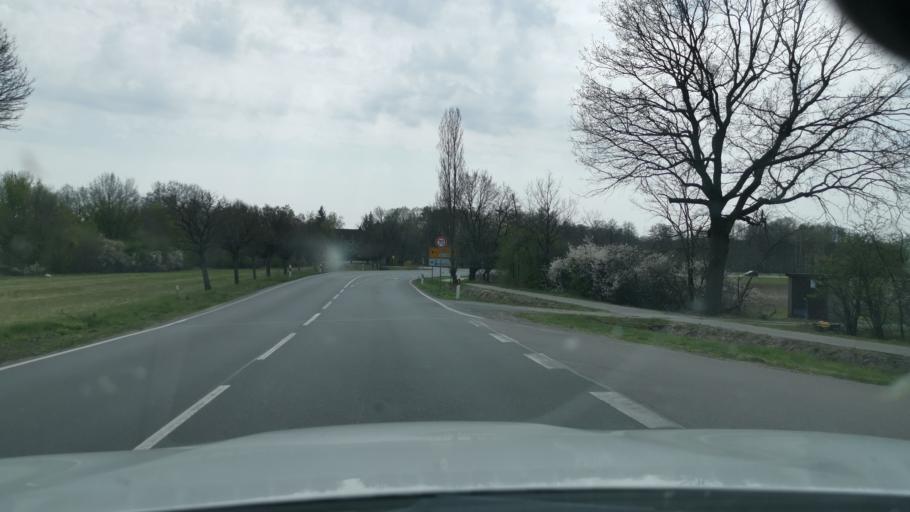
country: DE
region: Saxony
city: Bad Duben
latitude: 51.6060
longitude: 12.5862
